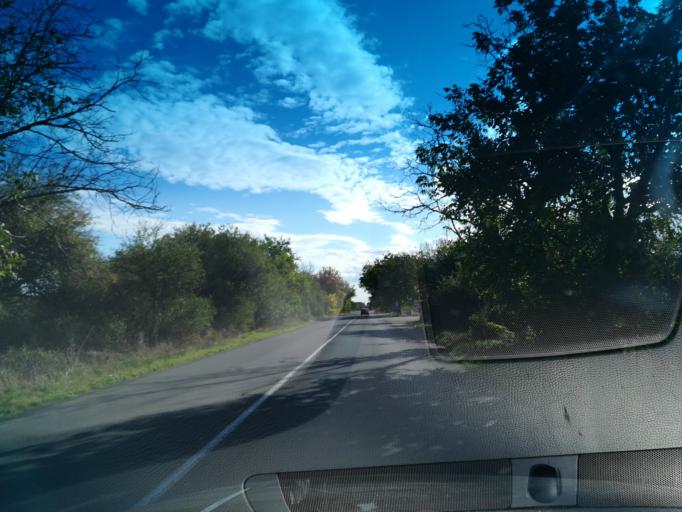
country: BG
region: Stara Zagora
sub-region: Obshtina Stara Zagora
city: Stara Zagora
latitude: 42.3696
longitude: 25.6534
